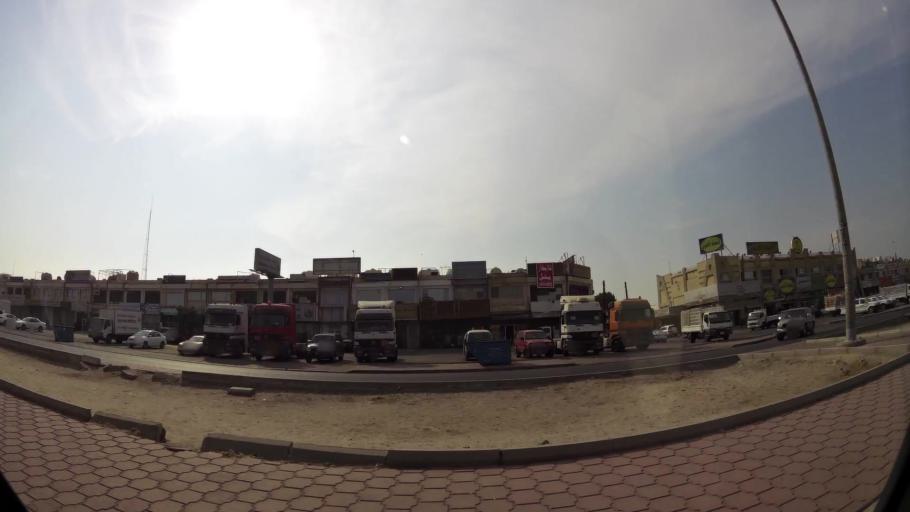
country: KW
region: Al Asimah
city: Ar Rabiyah
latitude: 29.3121
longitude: 47.9476
